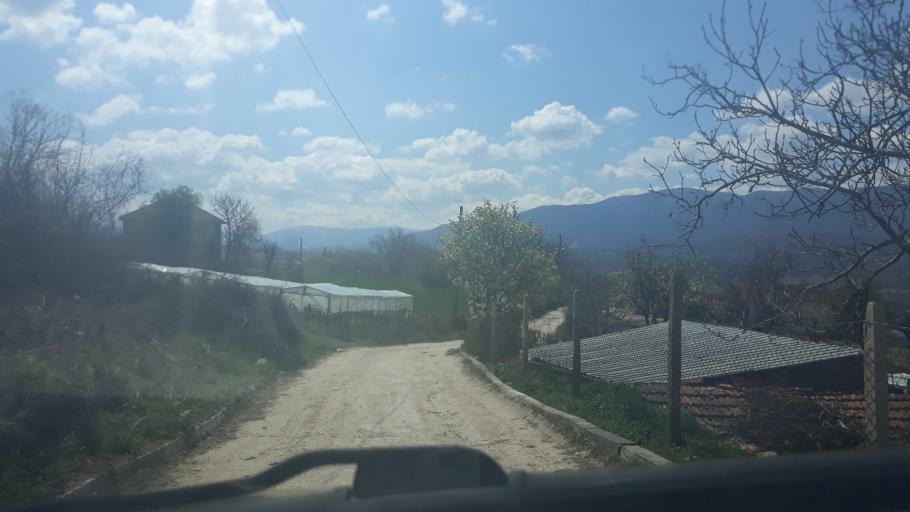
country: MK
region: Caska
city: Caska
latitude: 41.6493
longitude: 21.6957
